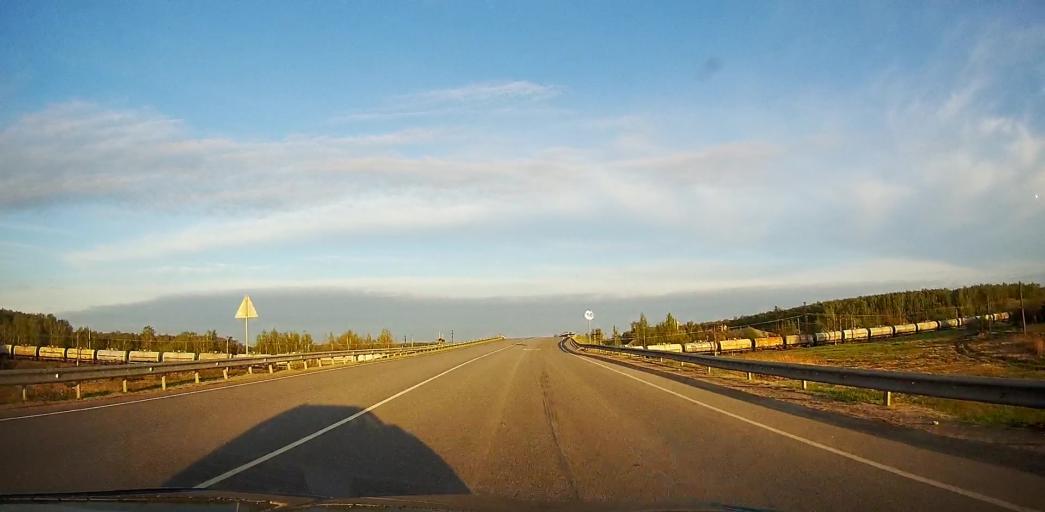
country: RU
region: Moskovskaya
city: Troitskoye
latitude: 55.2187
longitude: 38.5864
